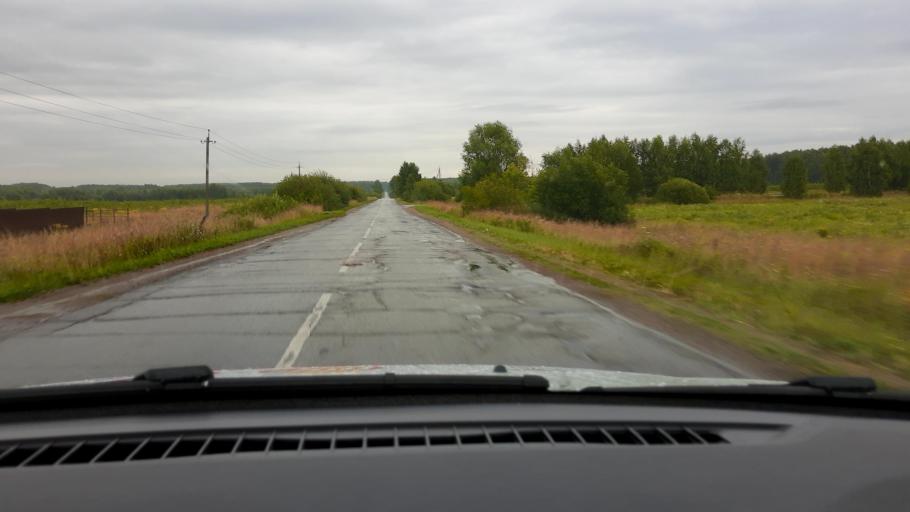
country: RU
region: Nizjnij Novgorod
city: Bogorodsk
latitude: 56.1056
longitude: 43.4314
